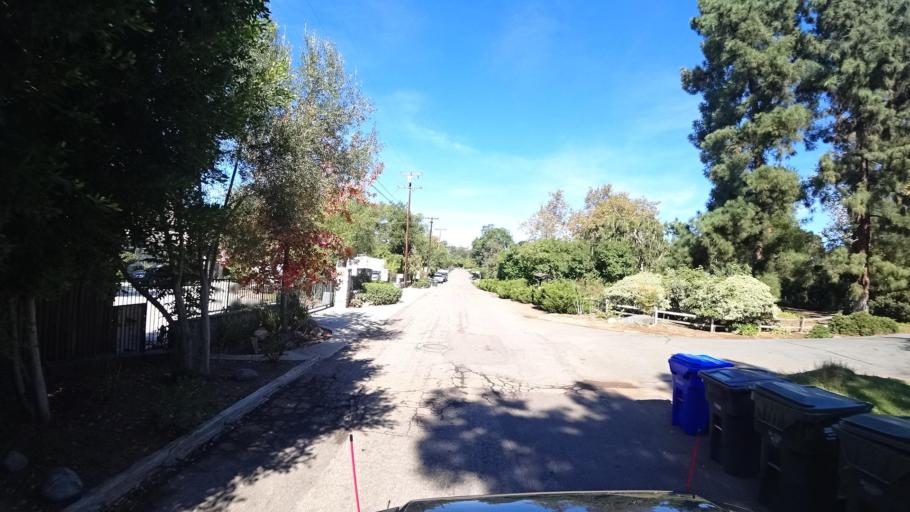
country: US
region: California
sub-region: San Diego County
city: Casa de Oro-Mount Helix
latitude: 32.7639
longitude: -116.9702
